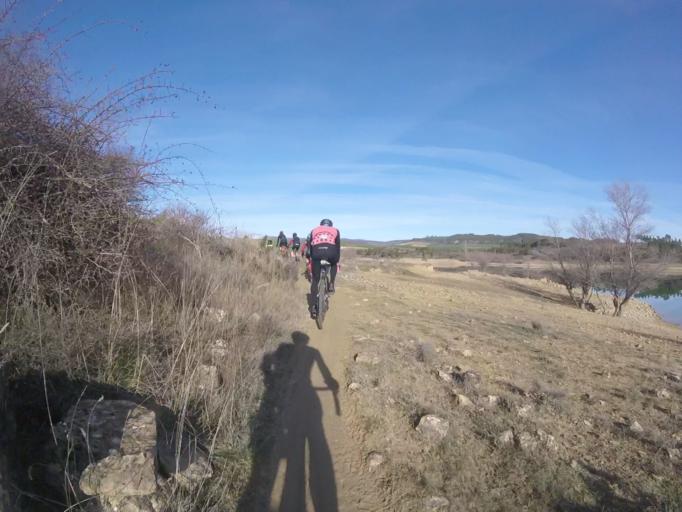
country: ES
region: Navarre
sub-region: Provincia de Navarra
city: Yerri
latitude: 42.7113
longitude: -1.9550
